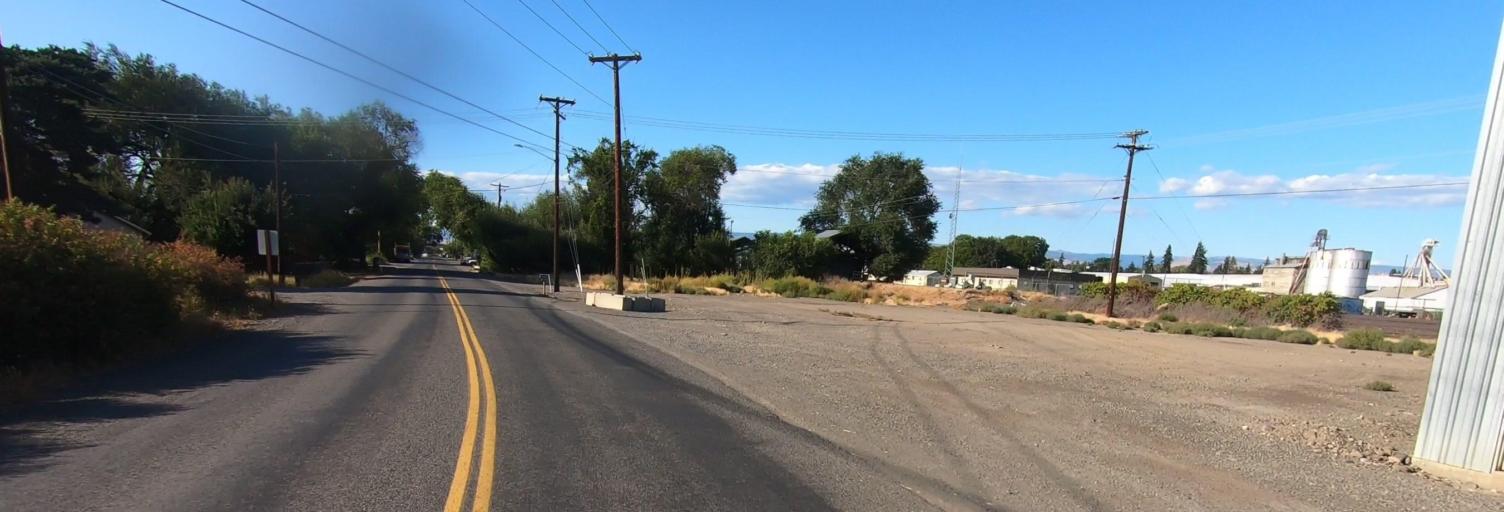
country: US
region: Washington
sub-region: Kittitas County
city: Ellensburg
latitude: 46.9916
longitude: -120.5552
